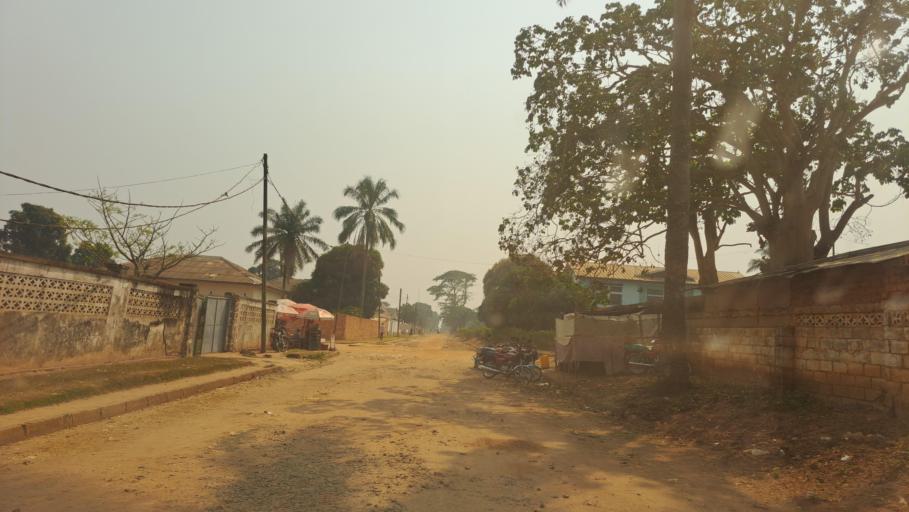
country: CD
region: Kasai-Occidental
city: Kananga
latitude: -5.9057
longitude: 22.4051
